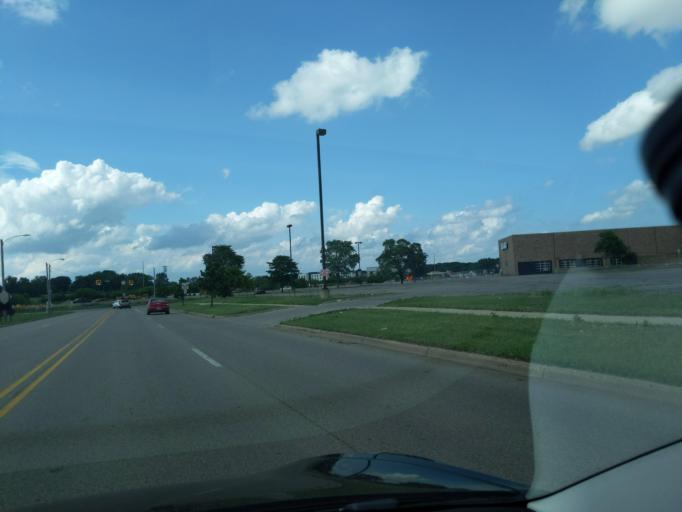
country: US
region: Michigan
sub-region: Jackson County
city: Jackson
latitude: 42.2689
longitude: -84.4330
